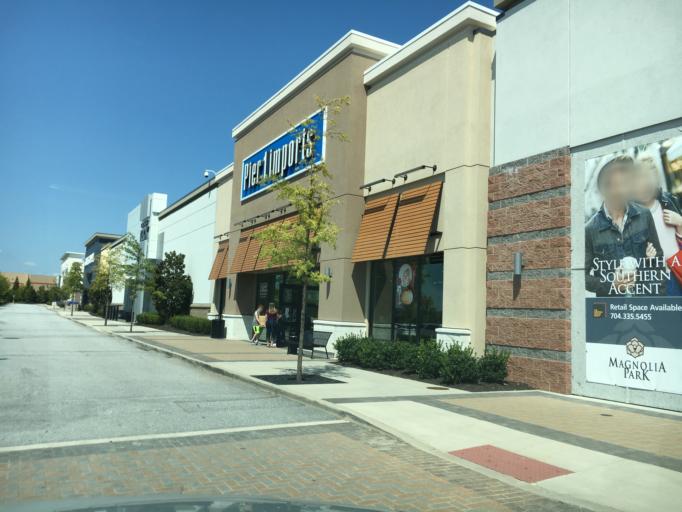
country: US
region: South Carolina
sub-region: Greenville County
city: Mauldin
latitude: 34.8348
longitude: -82.3074
